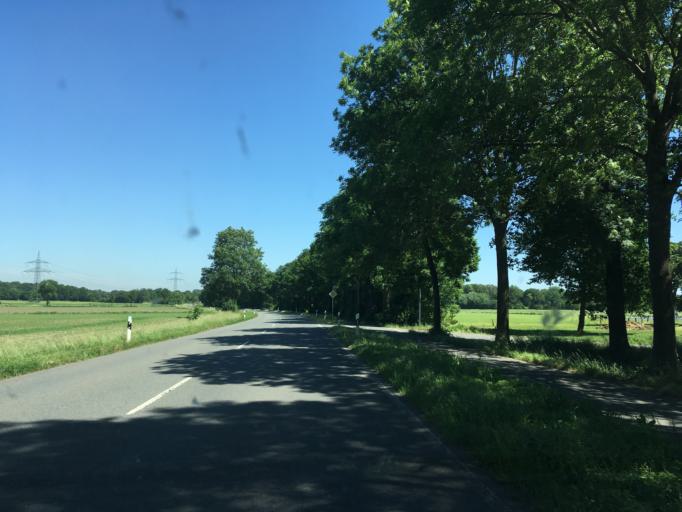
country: DE
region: North Rhine-Westphalia
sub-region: Regierungsbezirk Munster
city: Raesfeld
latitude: 51.7804
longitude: 6.8403
